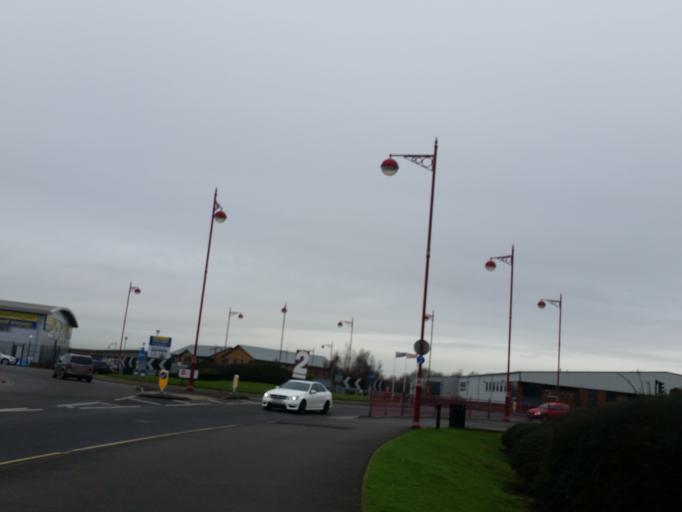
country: GB
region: England
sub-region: Derby
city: Derby
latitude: 52.9146
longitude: -1.4493
